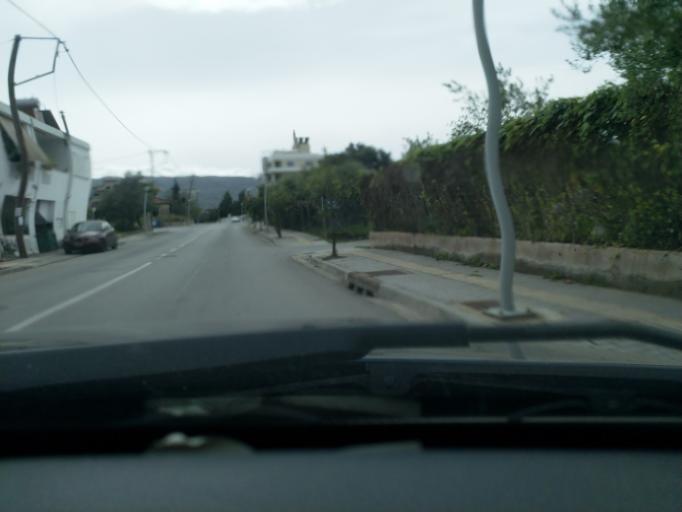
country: GR
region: Crete
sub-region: Nomos Chanias
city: Chania
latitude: 35.5001
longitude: 24.0216
